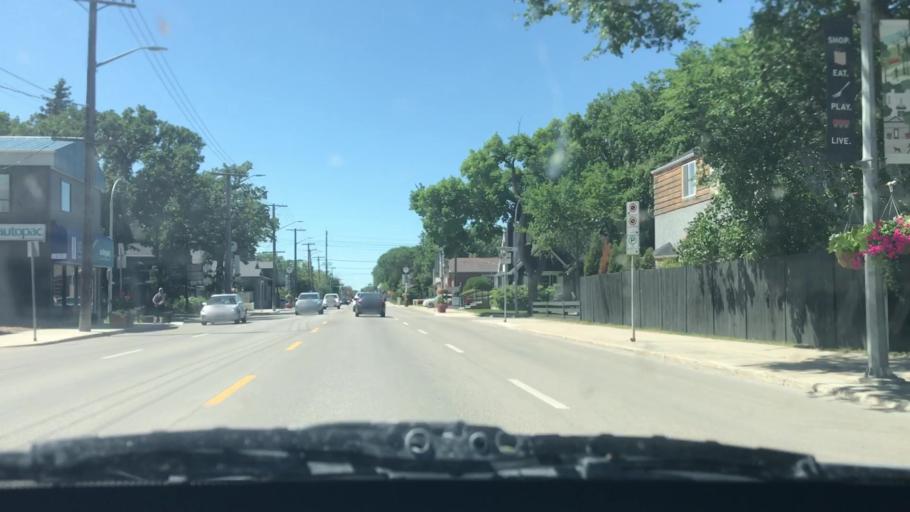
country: CA
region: Manitoba
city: Winnipeg
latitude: 49.8741
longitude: -97.1910
